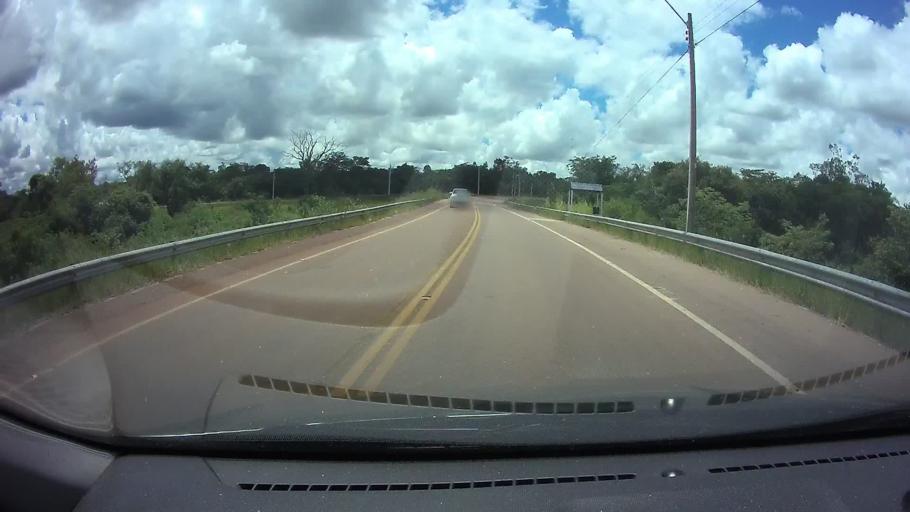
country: PY
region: Paraguari
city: La Colmena
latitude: -25.8927
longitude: -56.8320
